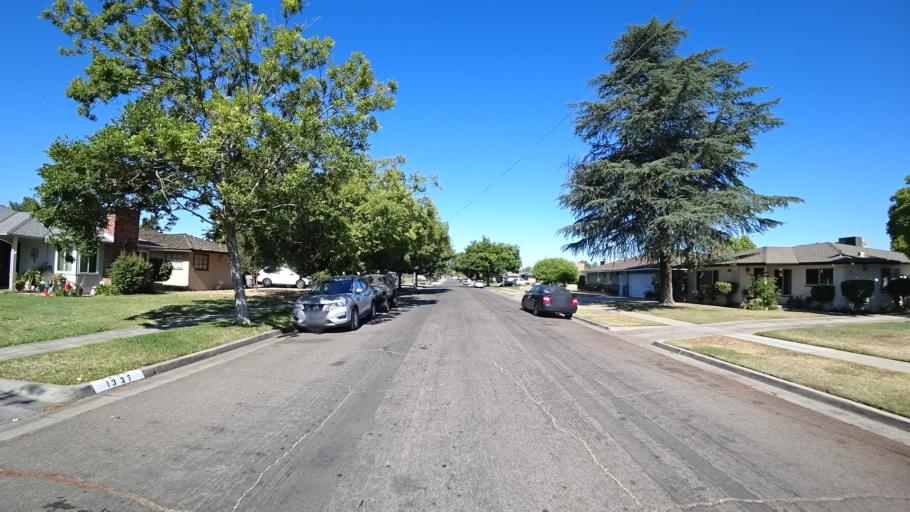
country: US
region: California
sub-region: Fresno County
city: Fresno
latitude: 36.7756
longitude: -119.8275
